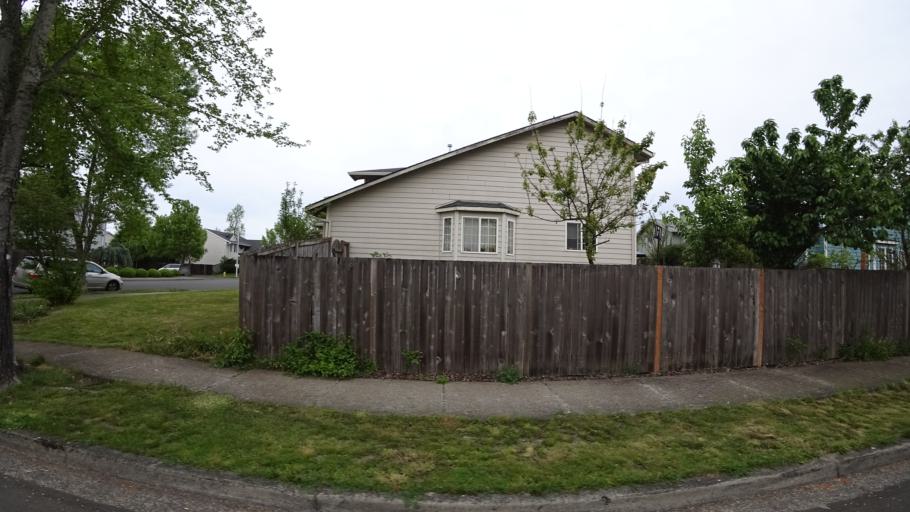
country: US
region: Oregon
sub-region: Washington County
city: Aloha
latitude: 45.5140
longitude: -122.9079
